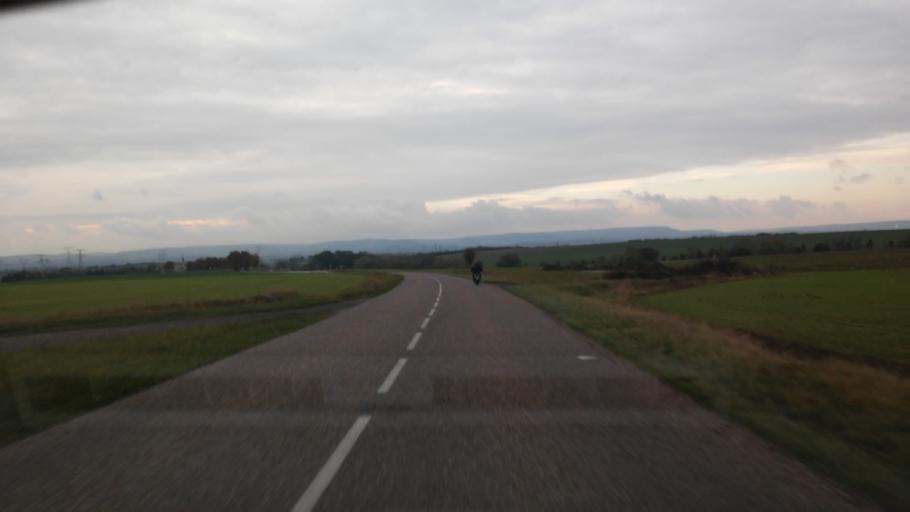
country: FR
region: Lorraine
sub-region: Departement de la Moselle
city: Vigy
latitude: 49.1984
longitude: 6.2672
